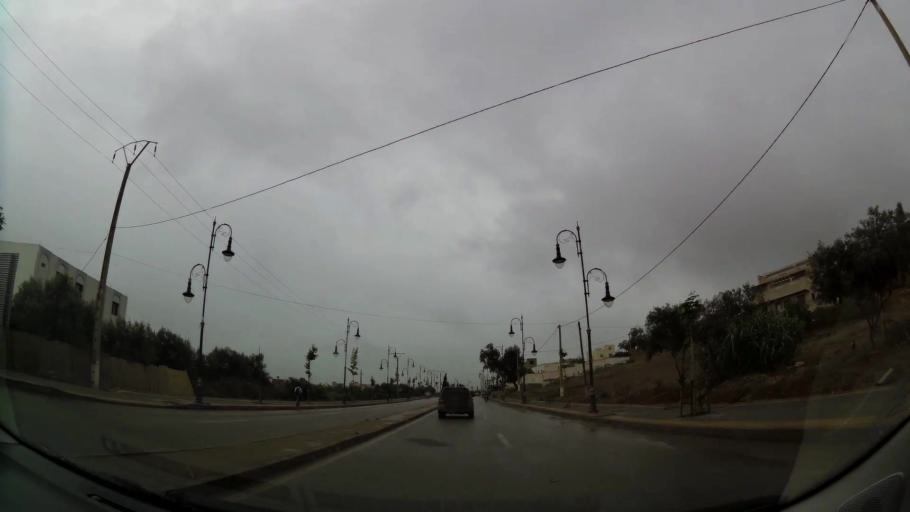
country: MA
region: Taza-Al Hoceima-Taounate
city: Imzourene
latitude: 35.1700
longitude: -3.8604
